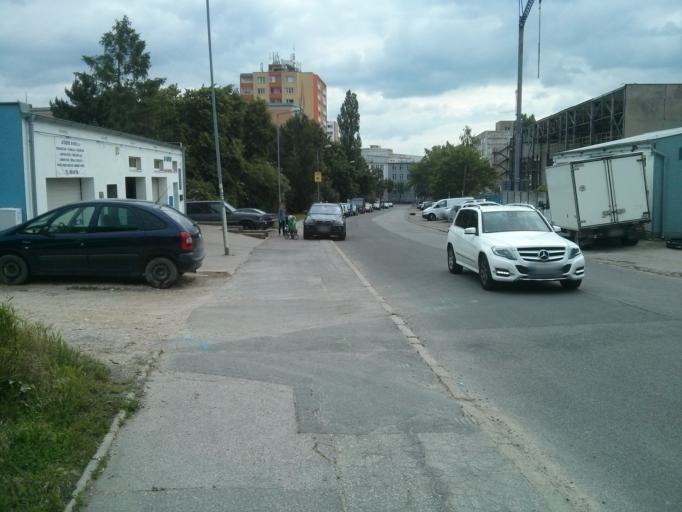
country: SK
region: Bratislavsky
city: Bratislava
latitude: 48.1728
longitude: 17.1237
